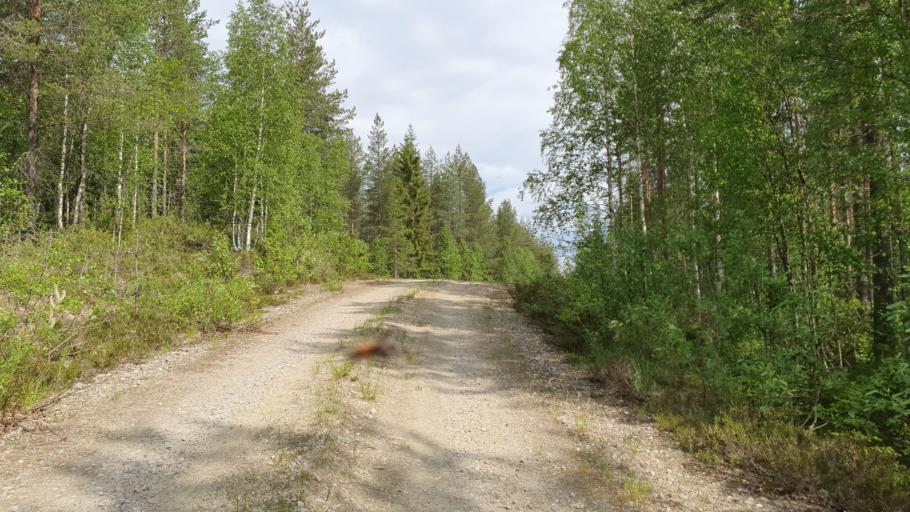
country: FI
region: Kainuu
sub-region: Kehys-Kainuu
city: Kuhmo
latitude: 64.4413
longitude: 29.6952
